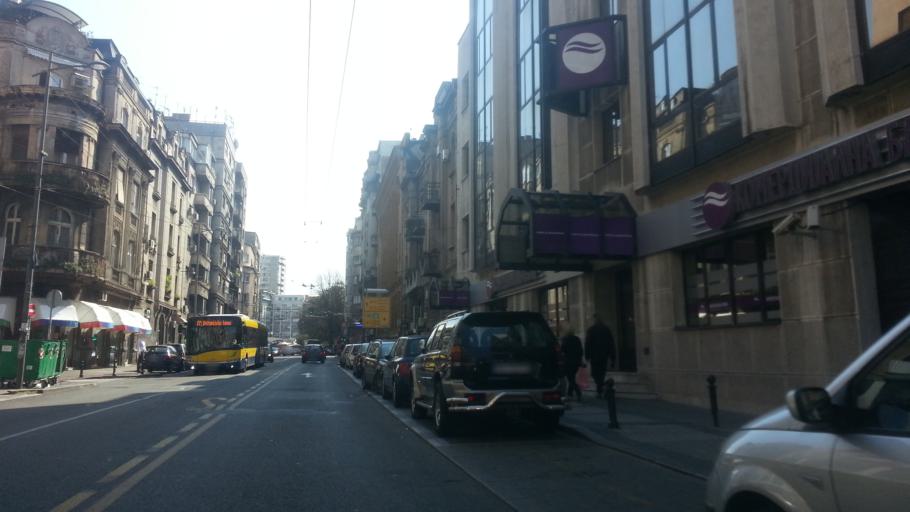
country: RS
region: Central Serbia
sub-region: Belgrade
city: Stari Grad
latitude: 44.8131
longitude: 20.4696
